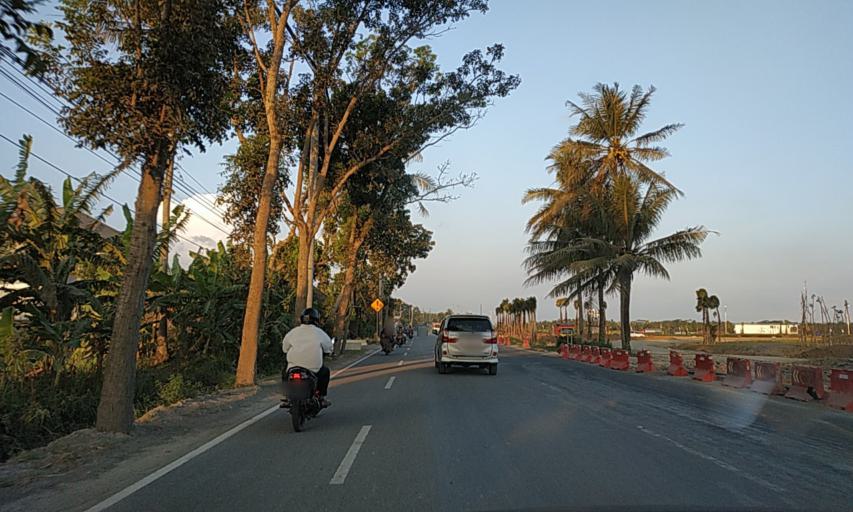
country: ID
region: Daerah Istimewa Yogyakarta
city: Srandakan
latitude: -7.8864
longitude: 110.0624
